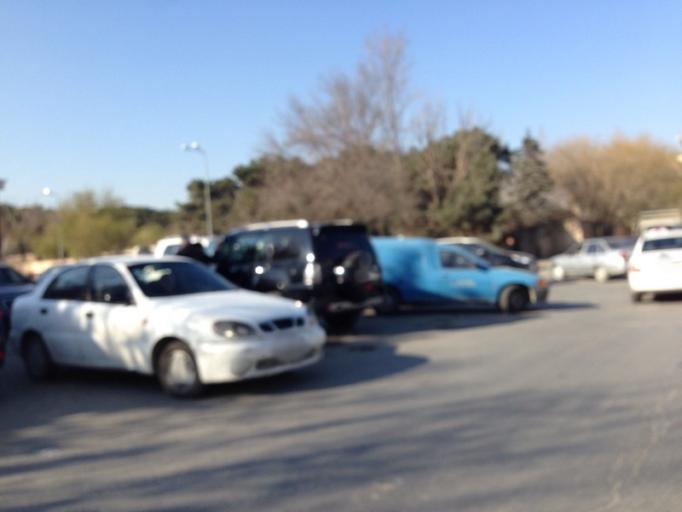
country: AZ
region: Baki
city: Baku
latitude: 40.4120
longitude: 49.8717
